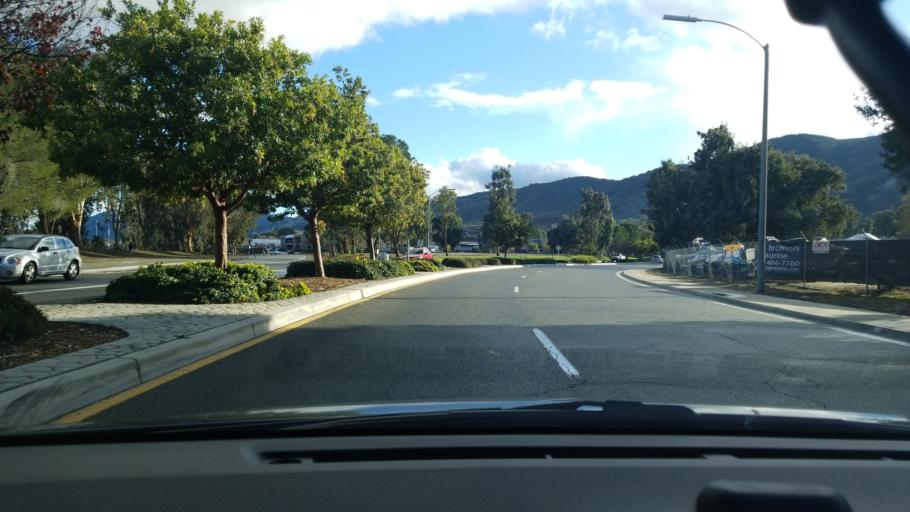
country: US
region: California
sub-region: Riverside County
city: Temecula
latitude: 33.5010
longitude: -117.1566
